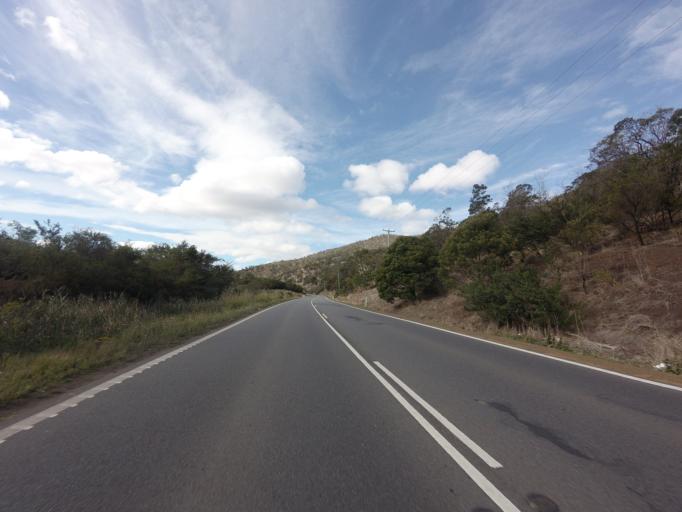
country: AU
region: Tasmania
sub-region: Derwent Valley
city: New Norfolk
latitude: -42.7719
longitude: 147.1383
